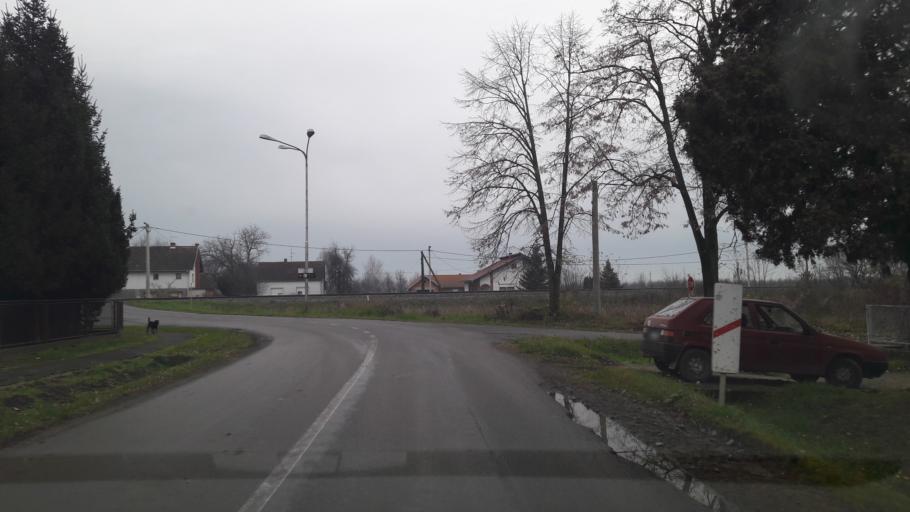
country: HR
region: Osjecko-Baranjska
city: Koska
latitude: 45.5416
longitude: 18.2917
